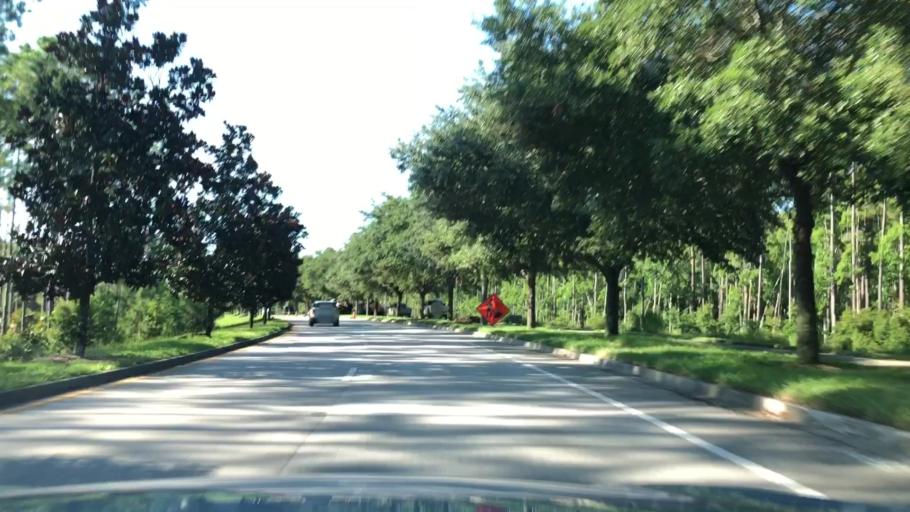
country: US
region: Florida
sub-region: Saint Johns County
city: Palm Valley
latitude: 30.0978
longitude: -81.4099
